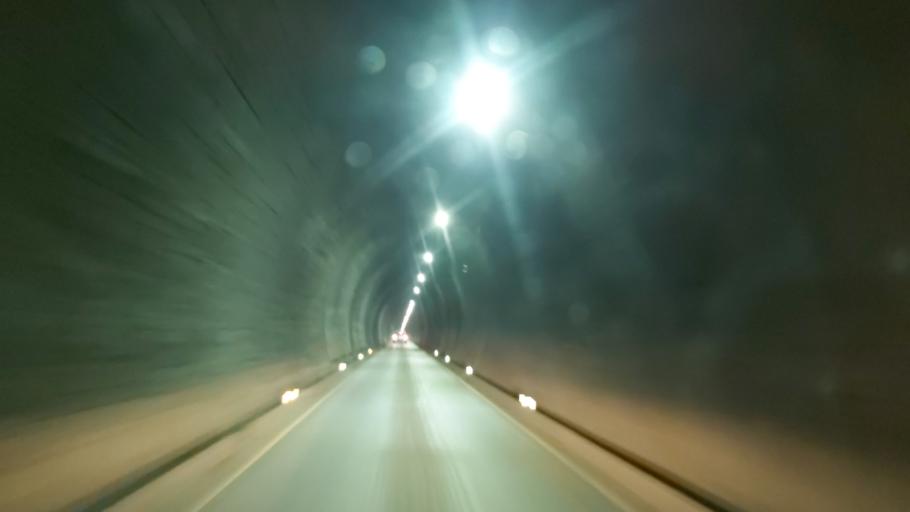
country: CL
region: Araucania
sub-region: Provincia de Cautin
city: Vilcun
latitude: -38.5342
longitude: -71.5090
